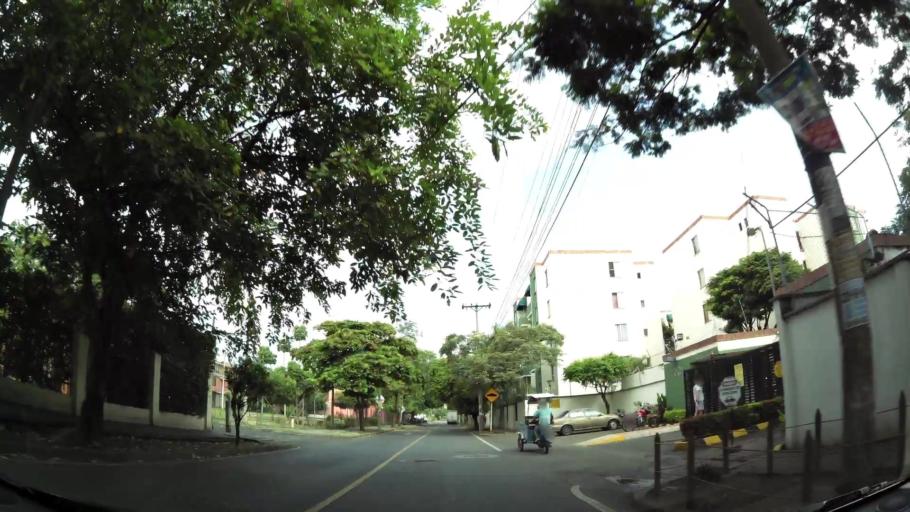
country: CO
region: Valle del Cauca
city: Cali
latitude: 3.4822
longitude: -76.4943
